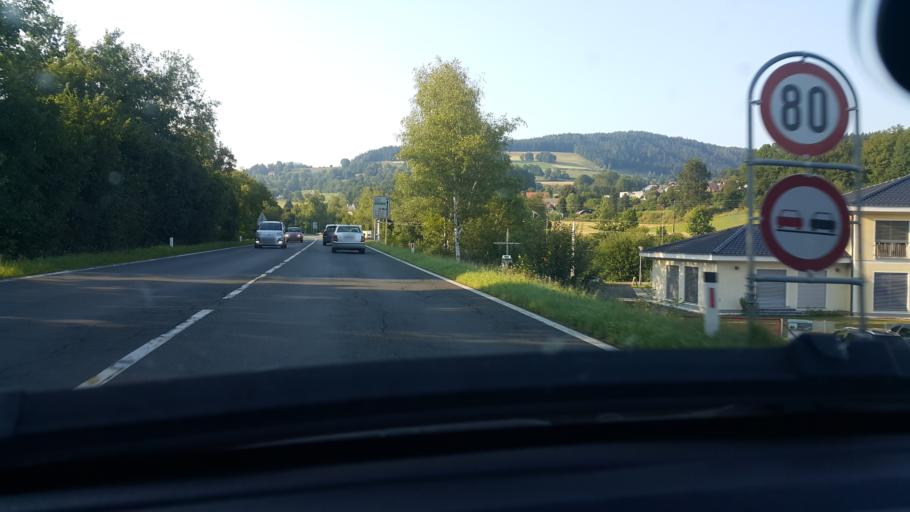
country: AT
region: Carinthia
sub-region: Politischer Bezirk Feldkirchen
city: Feldkirchen in Karnten
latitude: 46.7202
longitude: 14.1053
